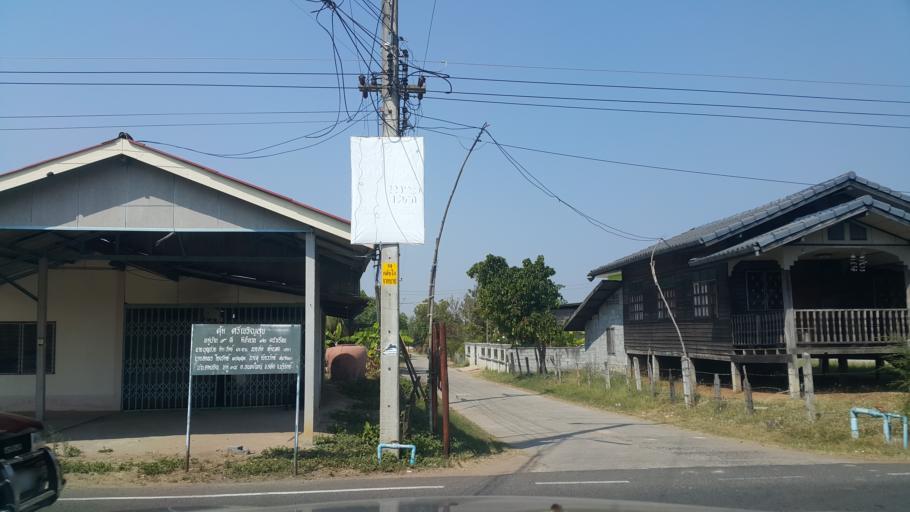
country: TH
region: Buriram
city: Satuek
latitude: 15.1480
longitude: 103.3318
